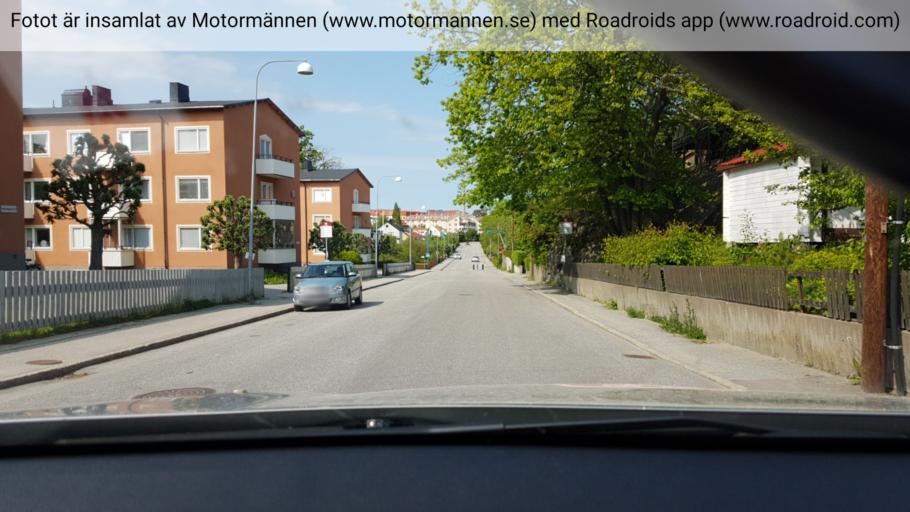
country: SE
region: Stockholm
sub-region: Nynashamns Kommun
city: Nynashamn
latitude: 58.9051
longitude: 17.9523
